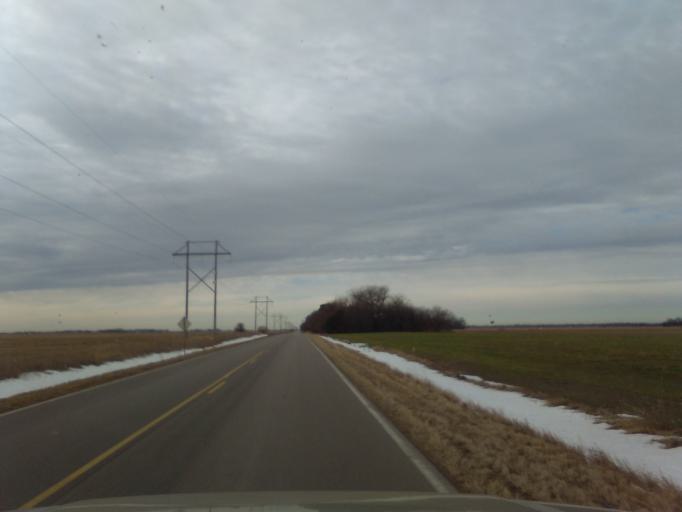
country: US
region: Nebraska
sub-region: Buffalo County
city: Gibbon
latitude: 40.6550
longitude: -98.8025
